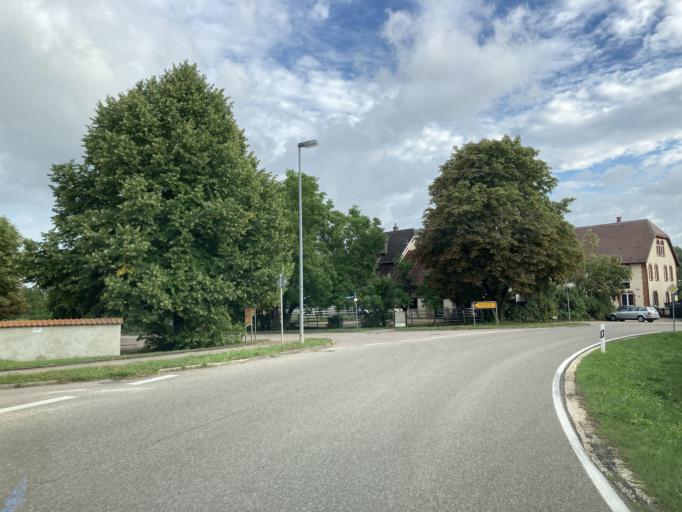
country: DE
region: Bavaria
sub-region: Swabia
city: Ziertheim
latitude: 48.6751
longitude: 10.3752
